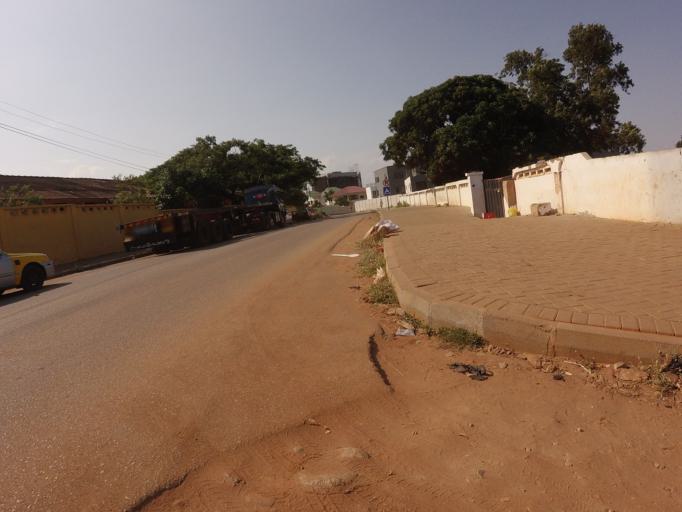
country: GH
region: Greater Accra
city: Accra
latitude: 5.5765
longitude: -0.1603
